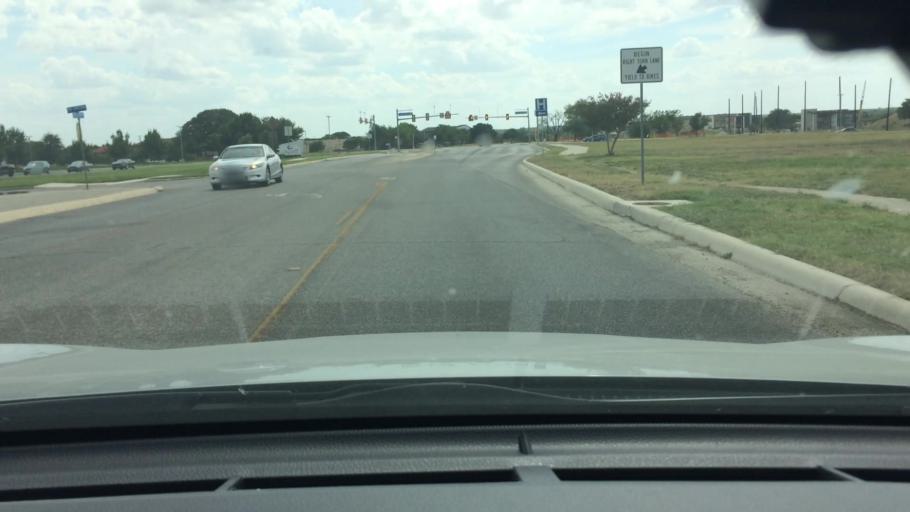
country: US
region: Texas
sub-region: Bexar County
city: San Antonio
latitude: 29.3468
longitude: -98.4436
